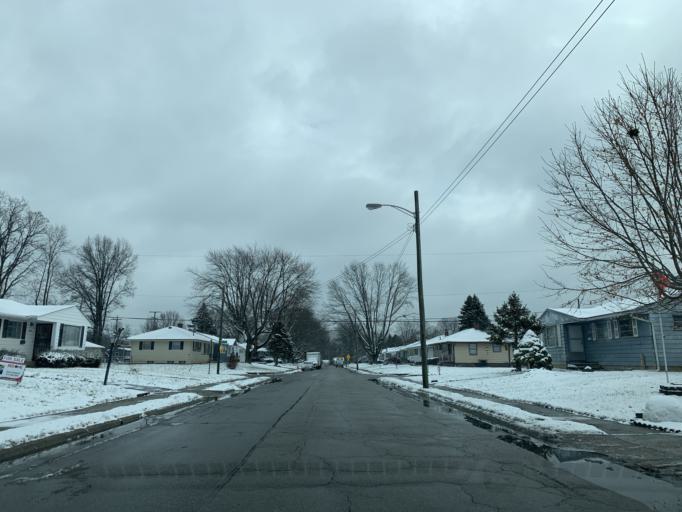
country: US
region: Ohio
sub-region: Franklin County
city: Minerva Park
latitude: 40.0540
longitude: -82.9663
